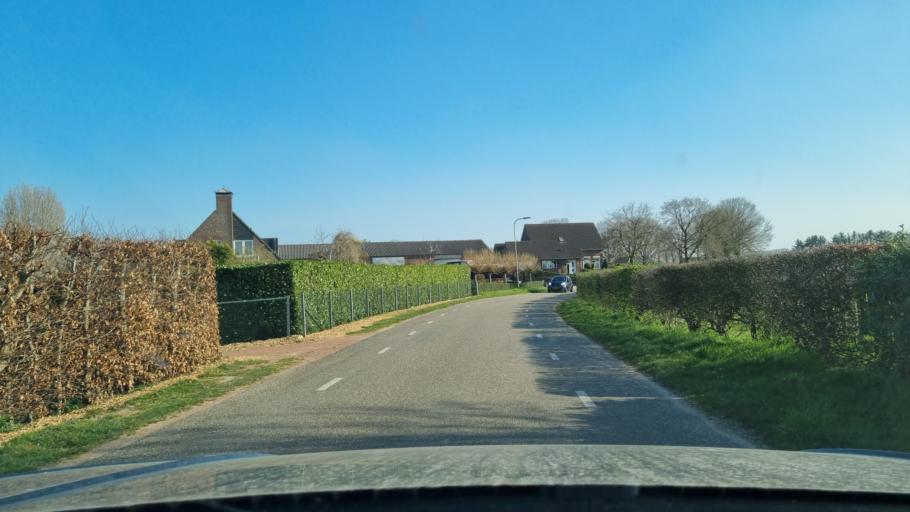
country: NL
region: North Brabant
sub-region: Gemeente Cuijk
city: Cuijk
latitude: 51.7354
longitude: 5.9019
